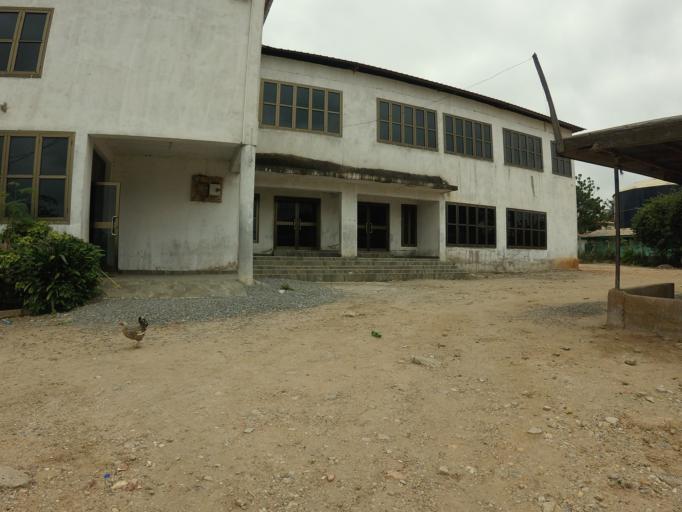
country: GH
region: Greater Accra
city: Dome
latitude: 5.6333
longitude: -0.2369
